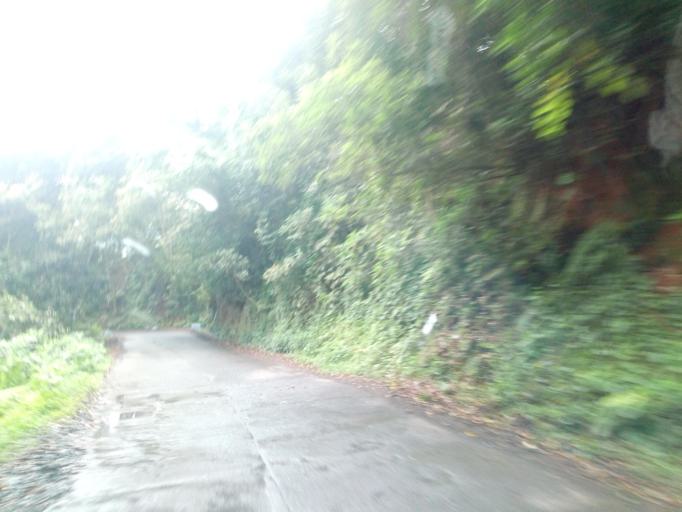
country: IN
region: Tamil Nadu
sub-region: Nilgiri
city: Wellington
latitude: 11.3624
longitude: 76.8380
